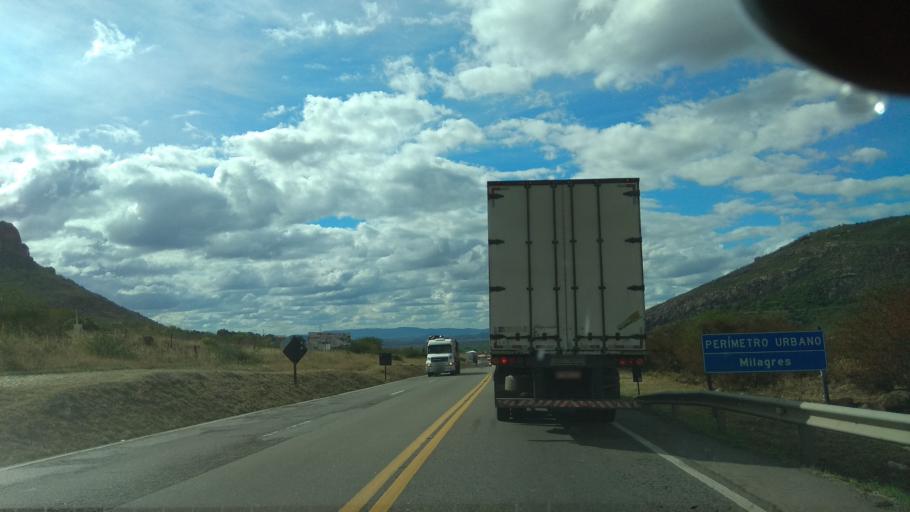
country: BR
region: Bahia
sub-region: Amargosa
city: Amargosa
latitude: -12.8832
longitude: -39.8588
